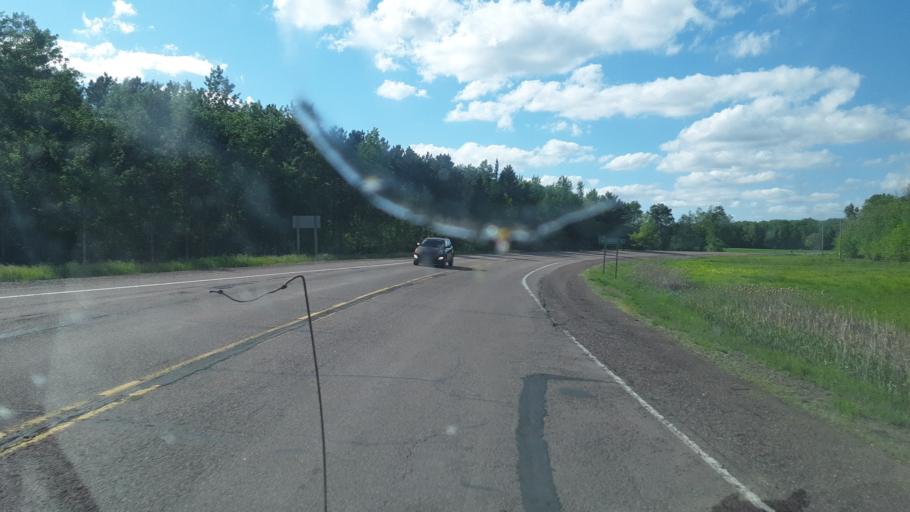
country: US
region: Wisconsin
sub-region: Wood County
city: Marshfield
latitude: 44.4548
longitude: -90.1800
